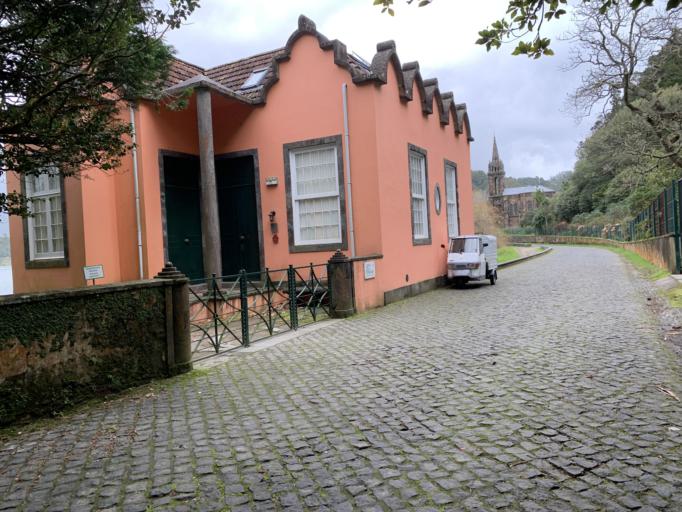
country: PT
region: Azores
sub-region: Povoacao
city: Furnas
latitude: 37.7503
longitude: -25.3324
